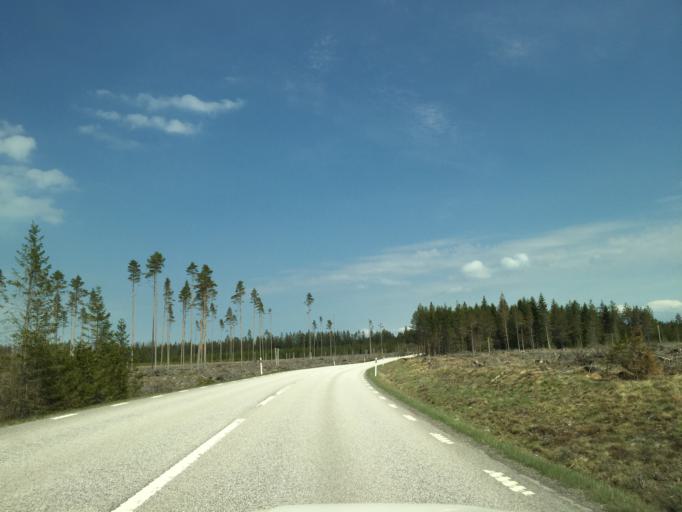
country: SE
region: Vaestra Goetaland
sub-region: Bengtsfors Kommun
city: Dals Langed
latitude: 58.8339
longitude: 12.1451
